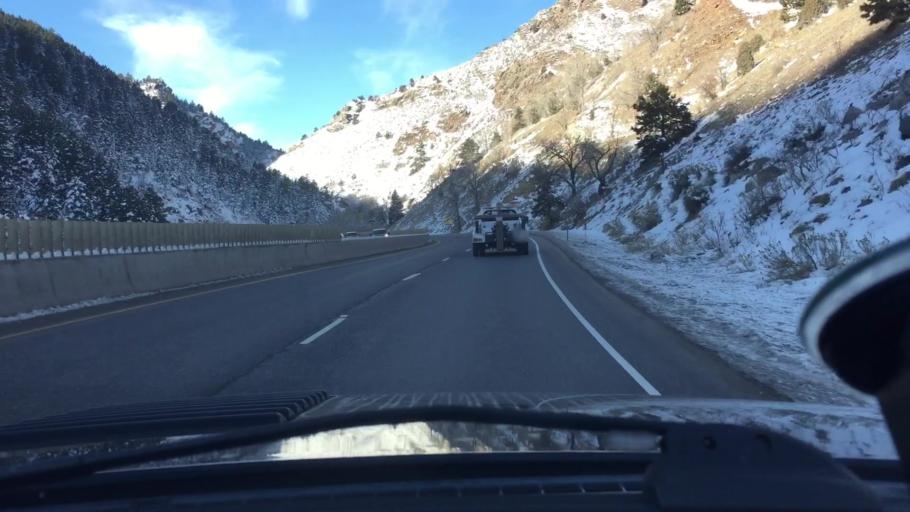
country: US
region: Colorado
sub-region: Jefferson County
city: Indian Hills
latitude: 39.6189
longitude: -105.2065
